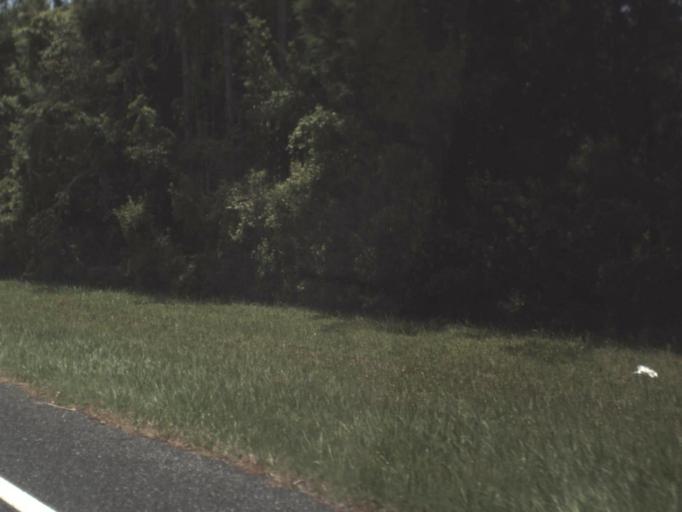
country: US
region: Florida
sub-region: Taylor County
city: Steinhatchee
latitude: 29.7125
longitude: -83.2984
